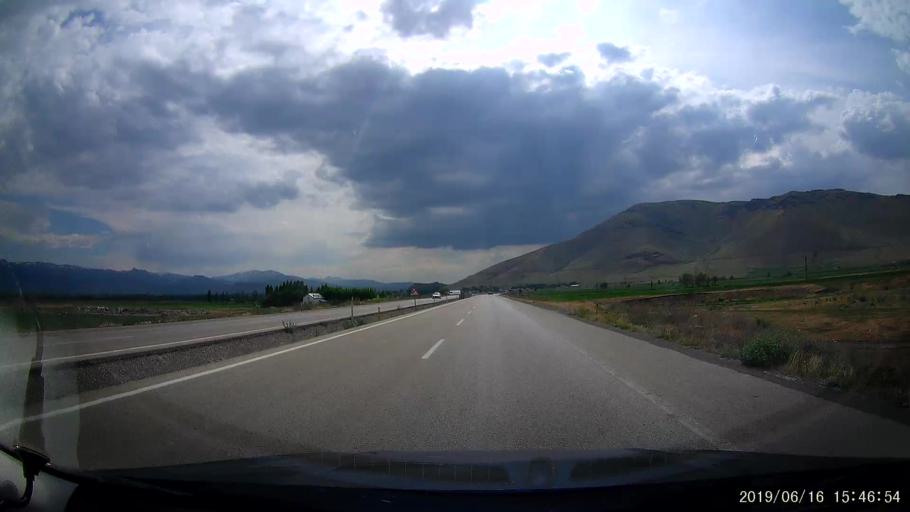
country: TR
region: Erzurum
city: Pasinler
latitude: 39.9893
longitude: 41.7336
